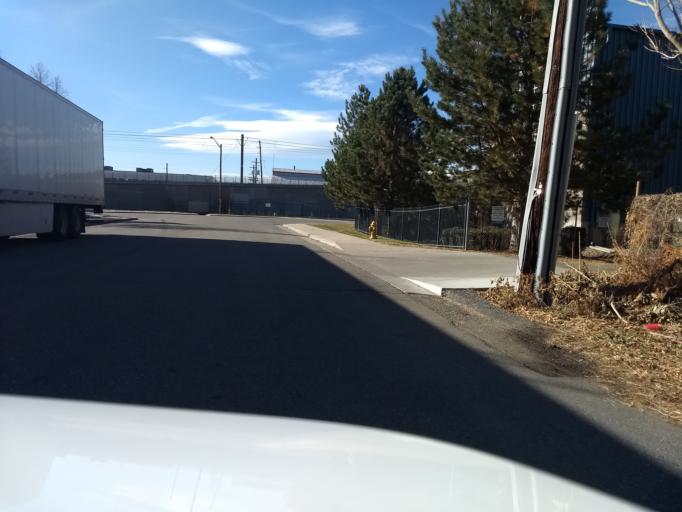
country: US
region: Colorado
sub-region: Denver County
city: Denver
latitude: 39.7166
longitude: -104.9969
